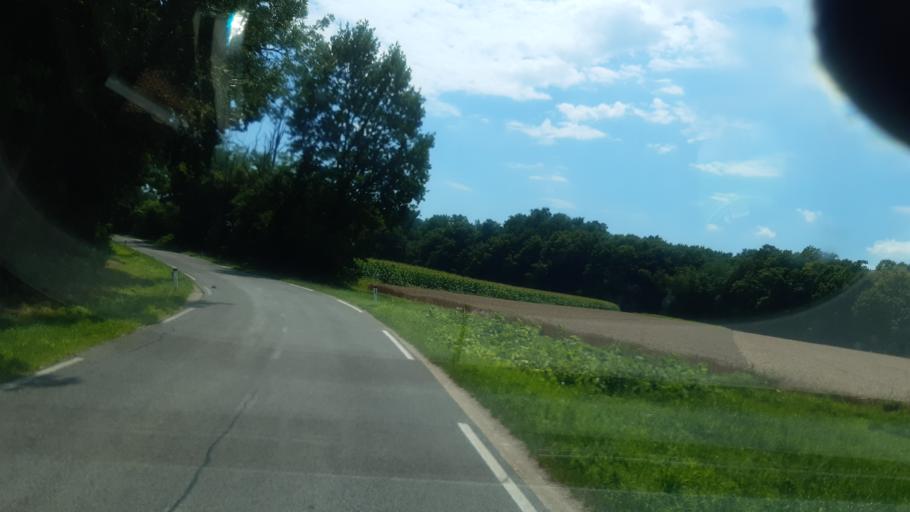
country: SI
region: Moravske Toplice
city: Moravske Toplice
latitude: 46.6655
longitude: 16.2310
